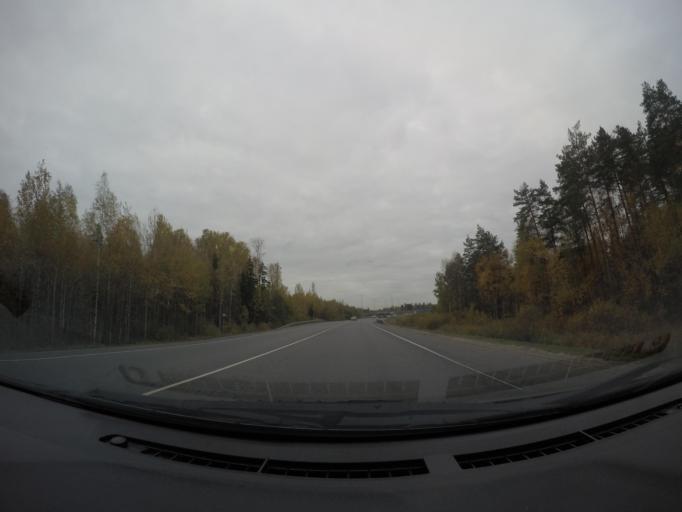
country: RU
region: Moskovskaya
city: Fryazevo
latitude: 55.7025
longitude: 38.4337
